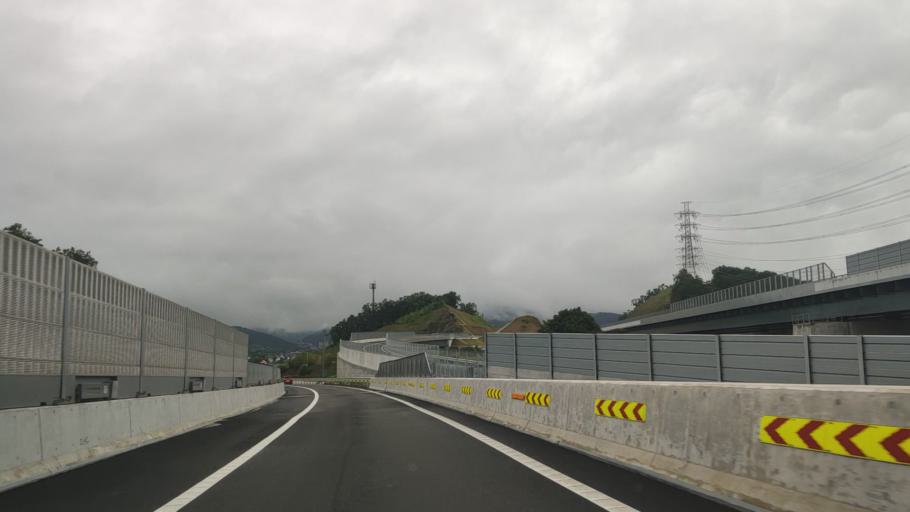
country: JP
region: Kanagawa
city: Isehara
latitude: 35.4113
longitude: 139.3111
